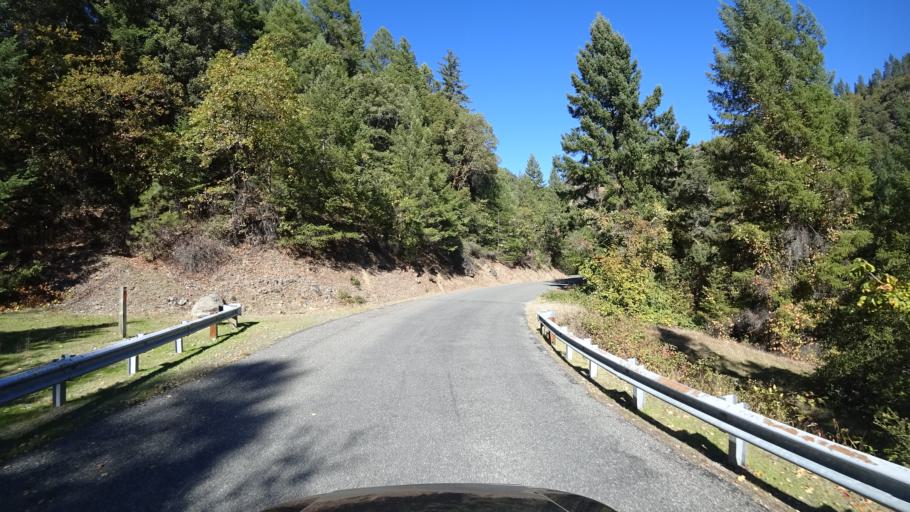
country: US
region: California
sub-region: Humboldt County
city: Willow Creek
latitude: 41.2538
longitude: -123.3170
